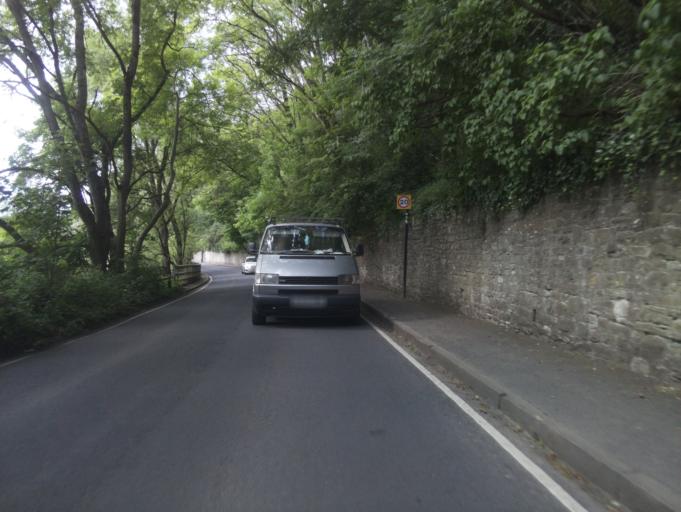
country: GB
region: England
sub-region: South Gloucestershire
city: Kingswood
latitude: 51.4489
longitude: -2.5339
